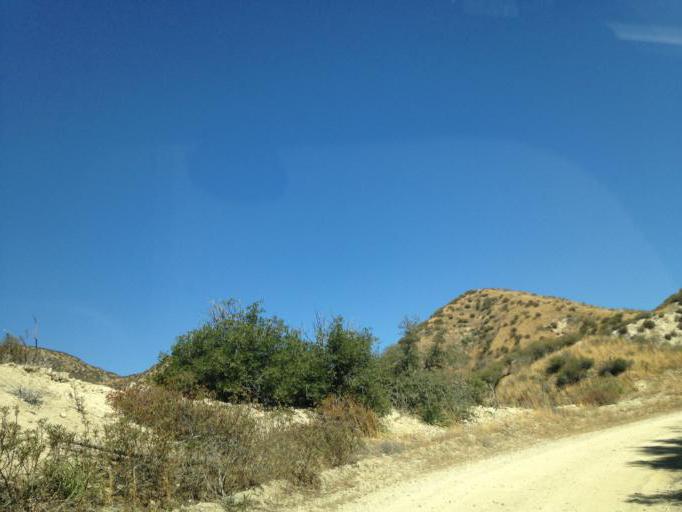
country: US
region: California
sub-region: San Bernardino County
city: Mentone
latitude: 34.1299
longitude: -117.1020
